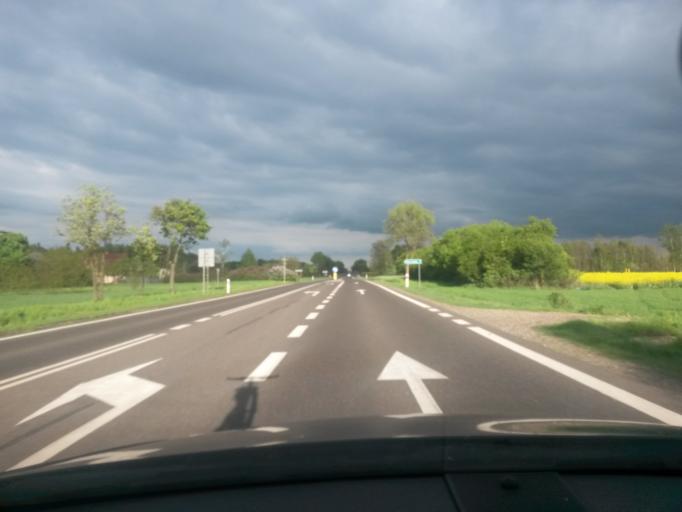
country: PL
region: Masovian Voivodeship
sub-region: Powiat plonski
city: Dzierzaznia
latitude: 52.6218
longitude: 20.2967
